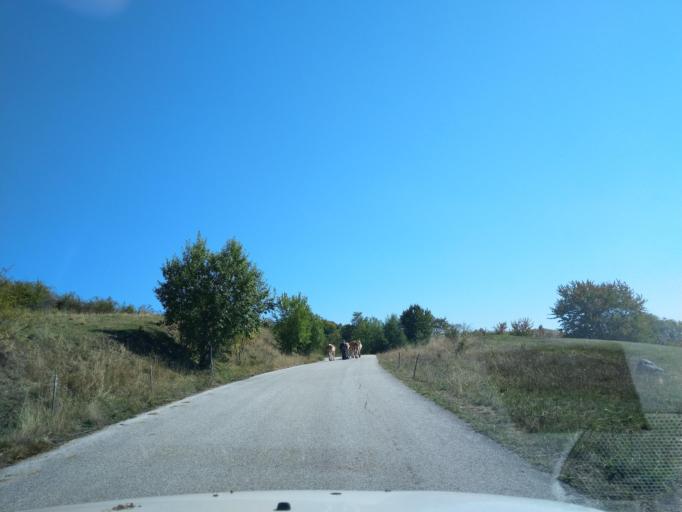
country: RS
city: Sokolovica
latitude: 43.2501
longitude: 20.3234
